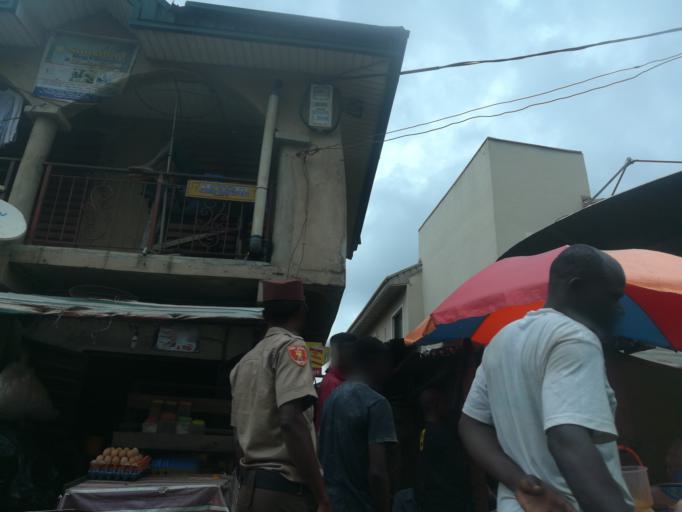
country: NG
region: Lagos
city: Ikeja
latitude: 6.6142
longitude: 3.3489
